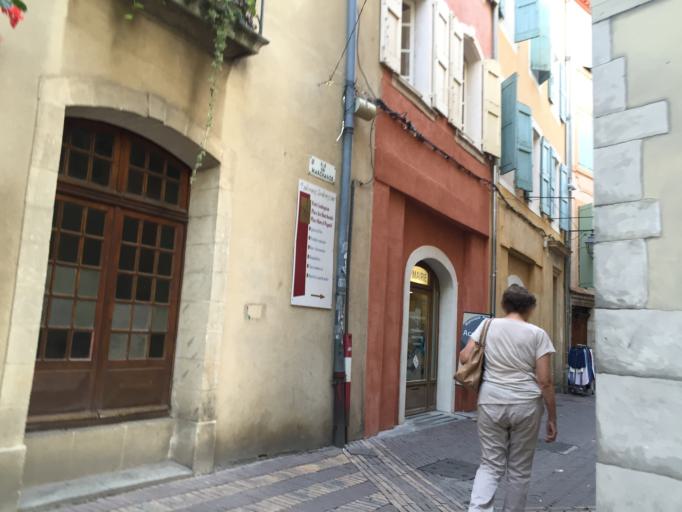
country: FR
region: Provence-Alpes-Cote d'Azur
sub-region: Departement des Alpes-de-Haute-Provence
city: Manosque
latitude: 43.8338
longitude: 5.7825
